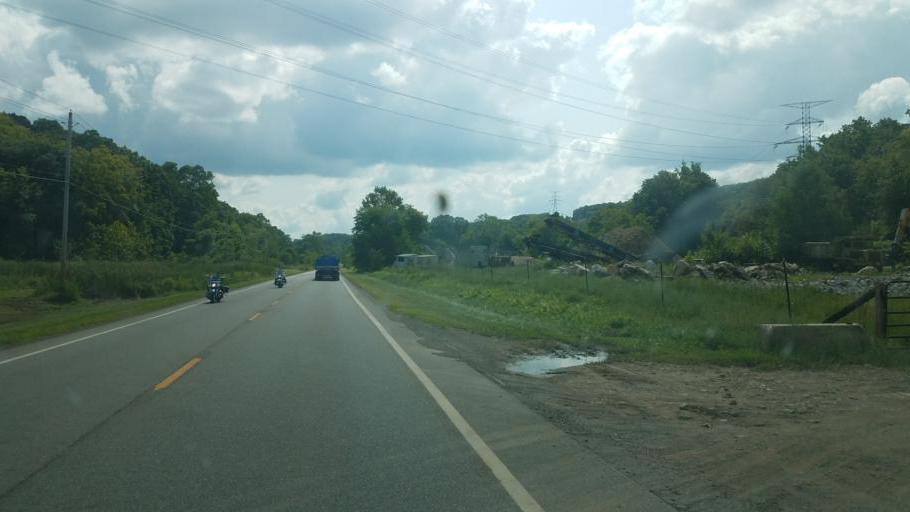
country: US
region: Ohio
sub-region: Columbiana County
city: Lisbon
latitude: 40.7682
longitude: -80.7393
